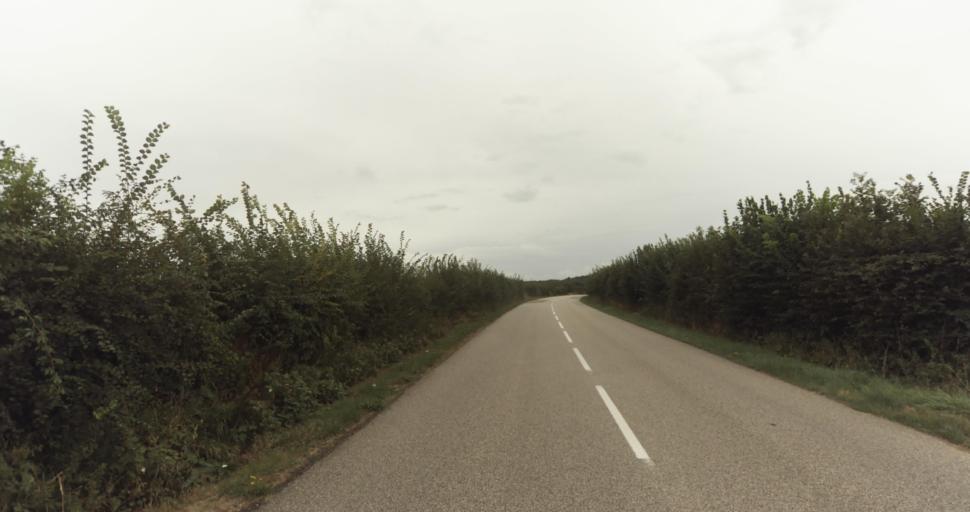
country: FR
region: Lower Normandy
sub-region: Departement de l'Orne
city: Gace
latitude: 48.8007
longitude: 0.3153
